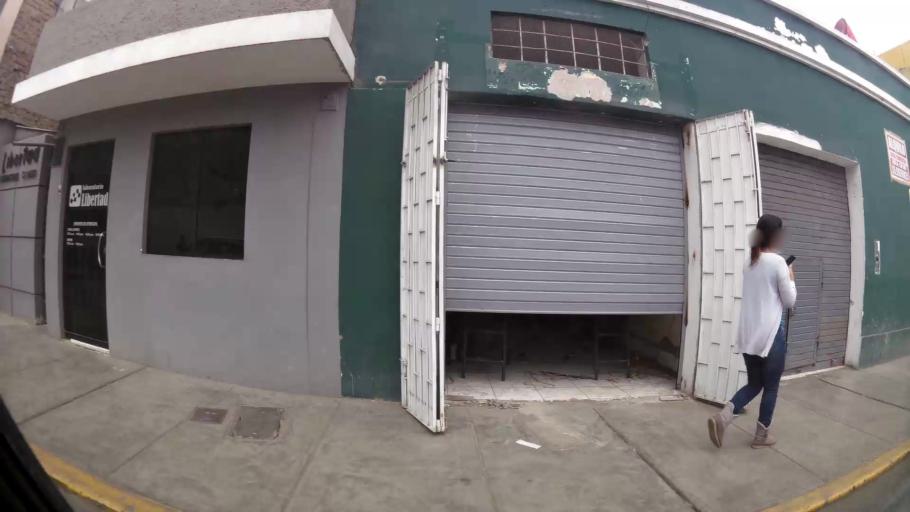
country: PE
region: La Libertad
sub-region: Provincia de Trujillo
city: Trujillo
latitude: -8.1157
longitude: -79.0281
